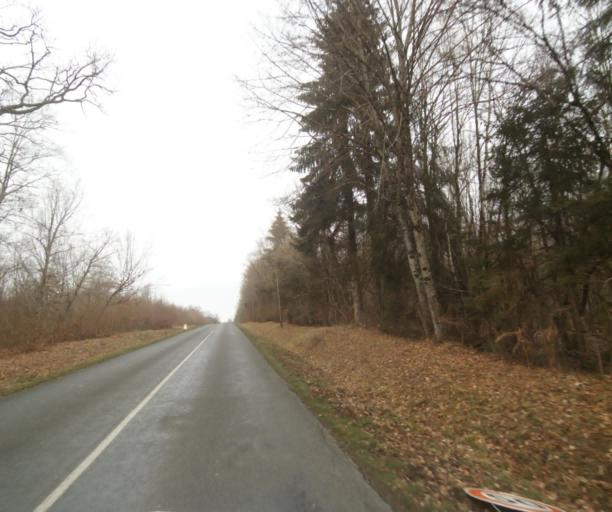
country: FR
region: Champagne-Ardenne
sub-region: Departement de la Haute-Marne
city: Villiers-en-Lieu
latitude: 48.6999
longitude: 4.8956
